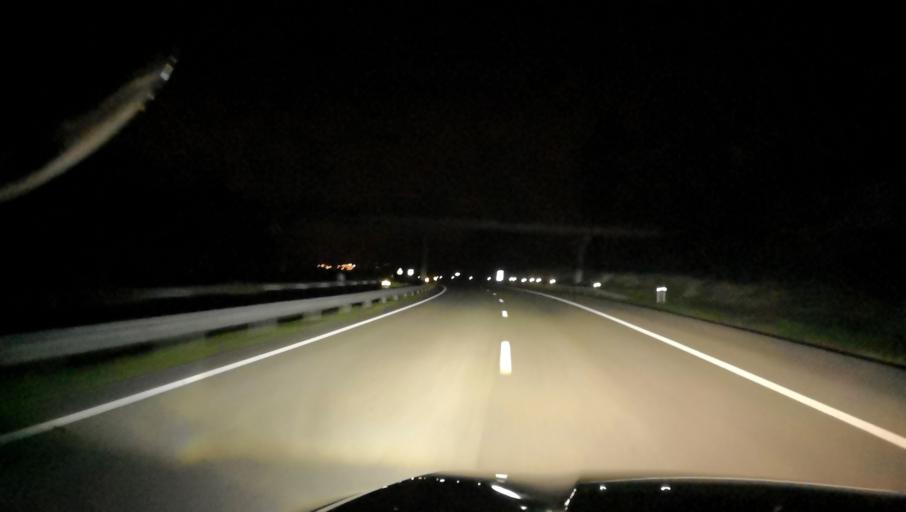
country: PT
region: Viseu
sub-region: Oliveira de Frades
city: Oliveira de Frades
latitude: 40.6827
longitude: -8.1862
